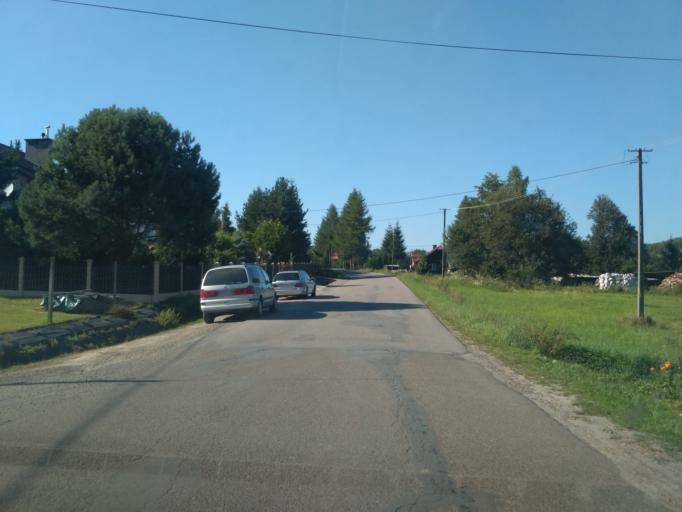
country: PL
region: Subcarpathian Voivodeship
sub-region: Powiat strzyzowski
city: Wysoka Strzyzowska
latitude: 49.8071
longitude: 21.7462
